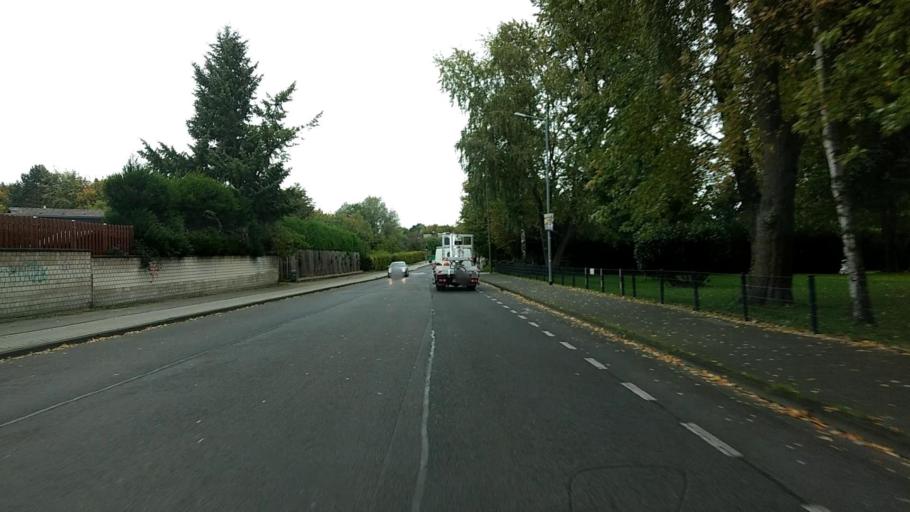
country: DE
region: North Rhine-Westphalia
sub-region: Regierungsbezirk Koln
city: Bergheim
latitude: 50.9478
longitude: 6.6294
